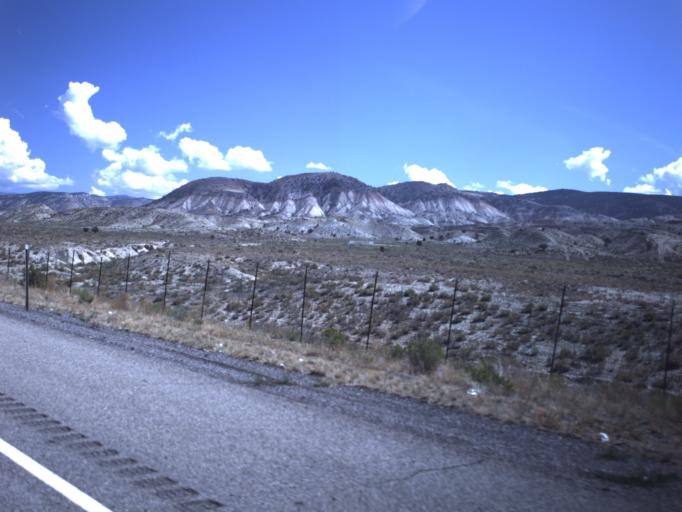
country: US
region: Utah
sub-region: Sevier County
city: Salina
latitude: 38.9154
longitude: -111.8826
